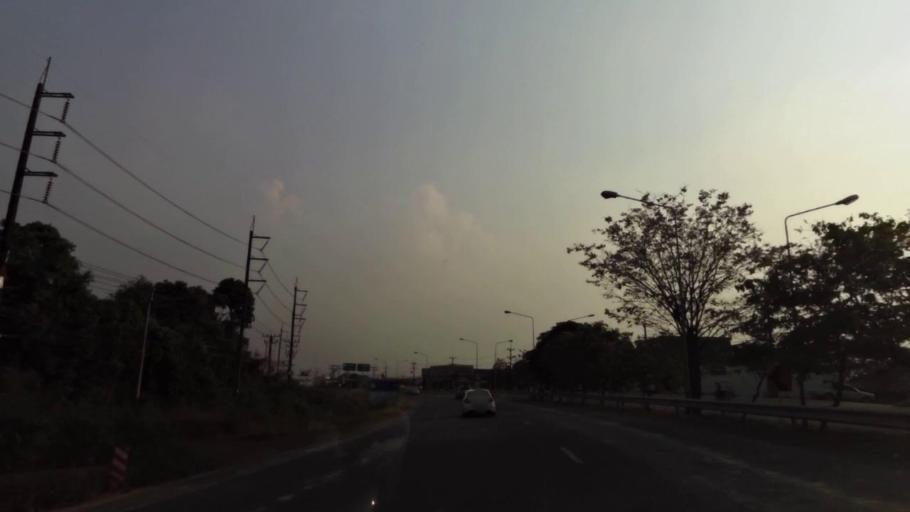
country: TH
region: Chanthaburi
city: Chanthaburi
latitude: 12.6058
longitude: 102.1338
